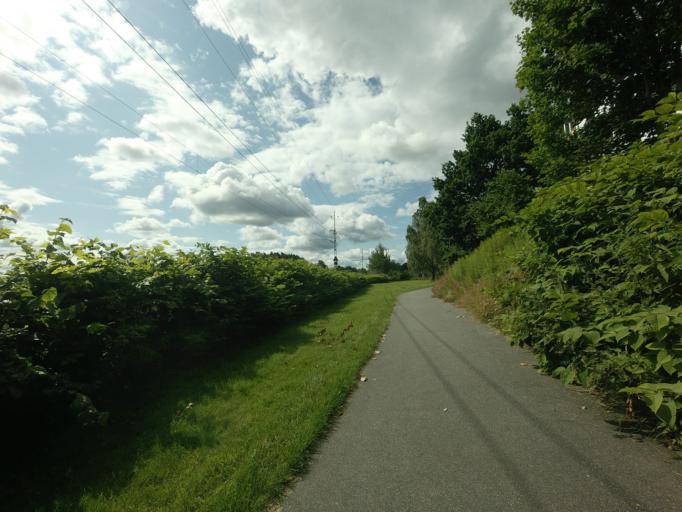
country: SE
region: Skane
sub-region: Hassleholms Kommun
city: Bjarnum
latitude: 56.3465
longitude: 13.6633
